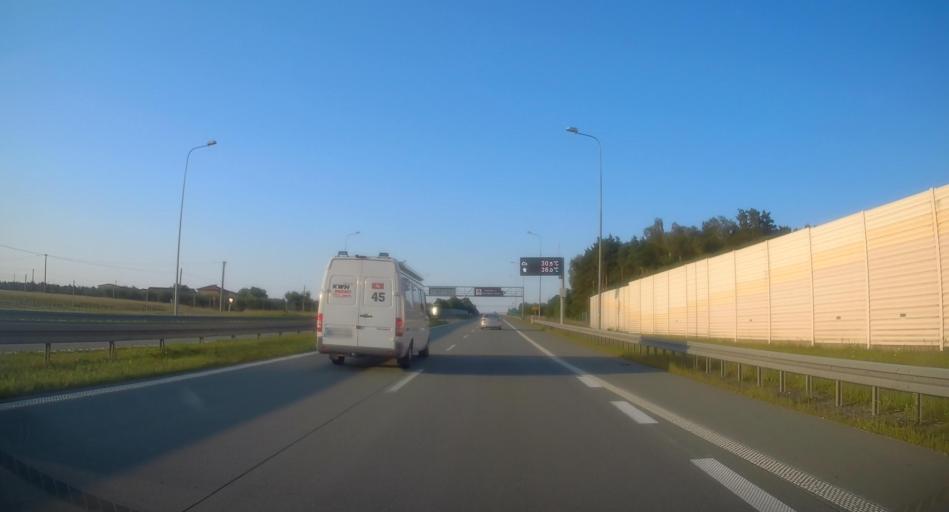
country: PL
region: Lodz Voivodeship
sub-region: Powiat skierniewicki
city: Kowiesy
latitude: 51.8942
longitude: 20.4263
